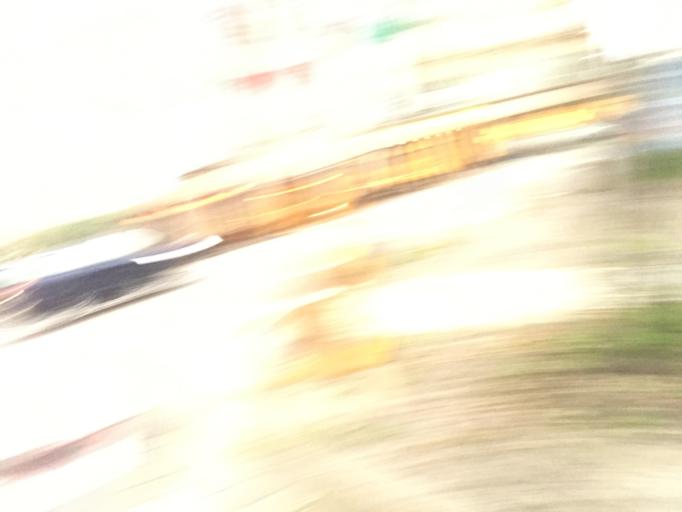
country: TW
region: Taiwan
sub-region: Yilan
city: Yilan
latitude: 24.7546
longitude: 121.7482
